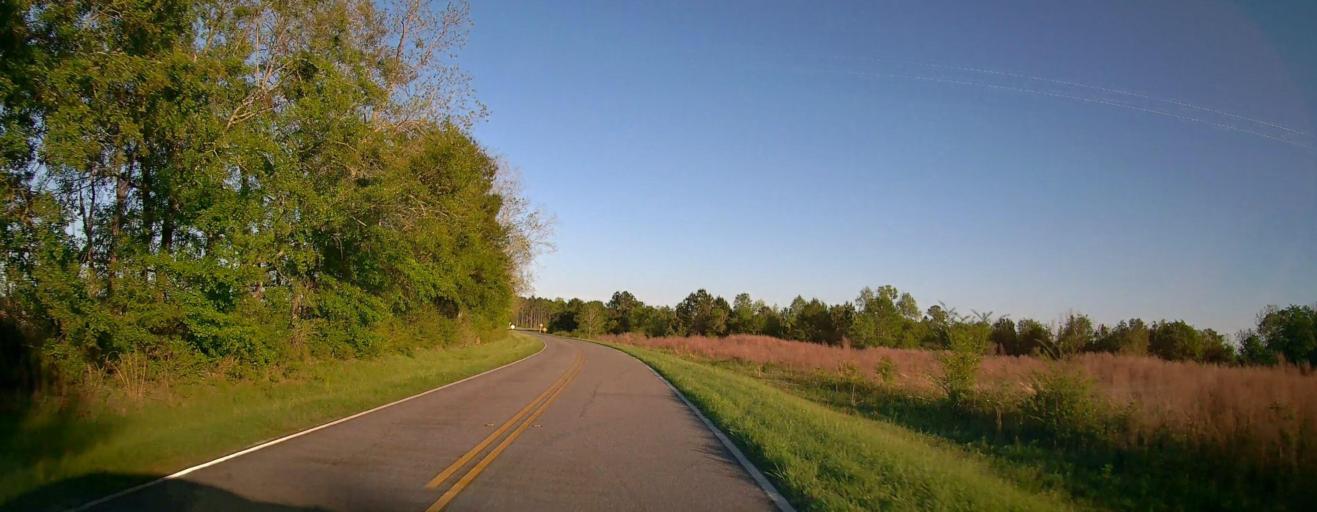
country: US
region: Georgia
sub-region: Ben Hill County
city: Fitzgerald
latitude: 31.6809
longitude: -83.2232
